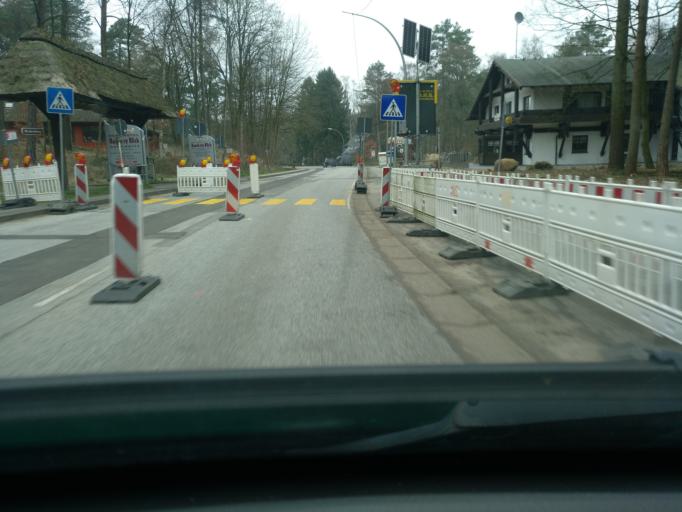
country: DE
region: Hamburg
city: Harburg
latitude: 53.4604
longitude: 9.8921
